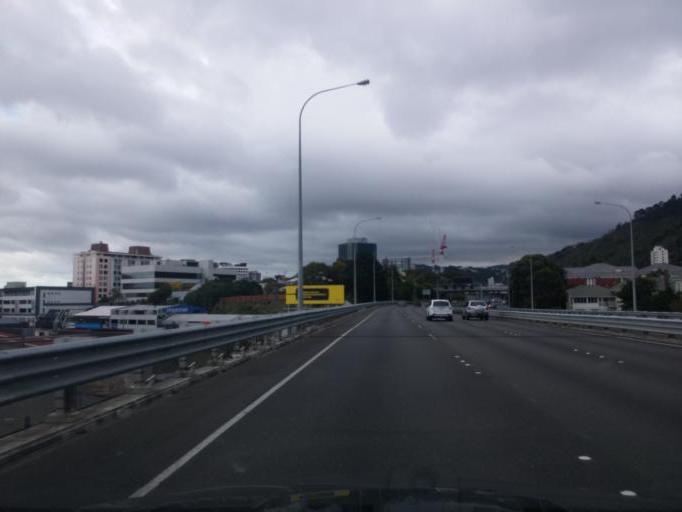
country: NZ
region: Wellington
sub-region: Wellington City
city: Wellington
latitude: -41.2690
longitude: 174.7819
